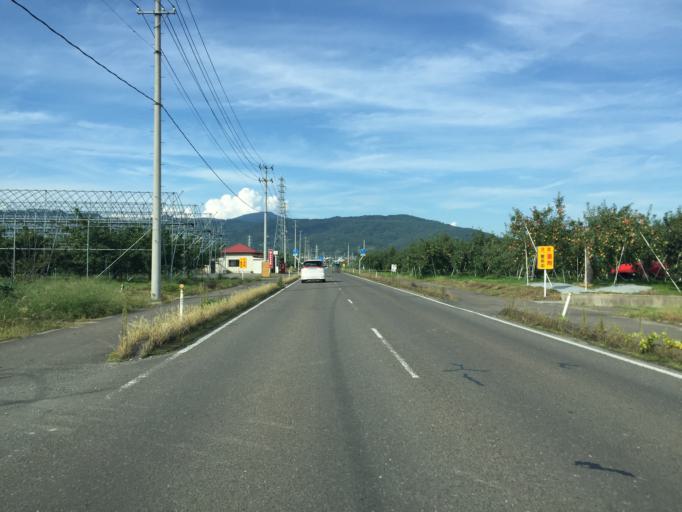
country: JP
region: Fukushima
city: Fukushima-shi
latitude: 37.8100
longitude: 140.4603
